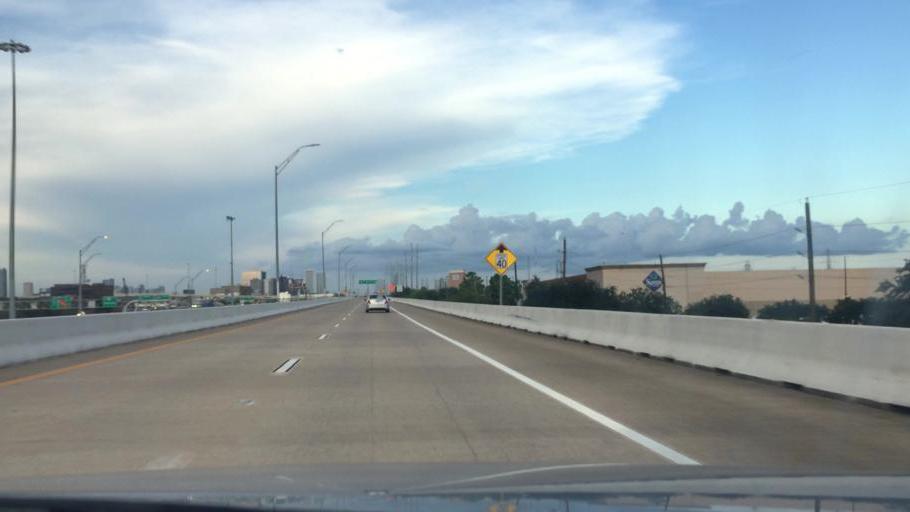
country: US
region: Texas
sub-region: Harris County
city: Bellaire
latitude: 29.7250
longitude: -95.4735
